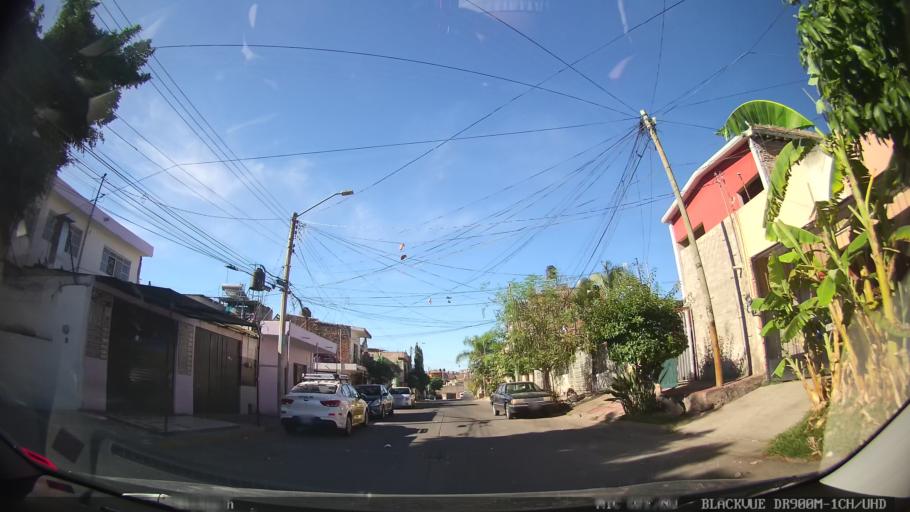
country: MX
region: Jalisco
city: Tlaquepaque
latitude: 20.6903
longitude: -103.2718
